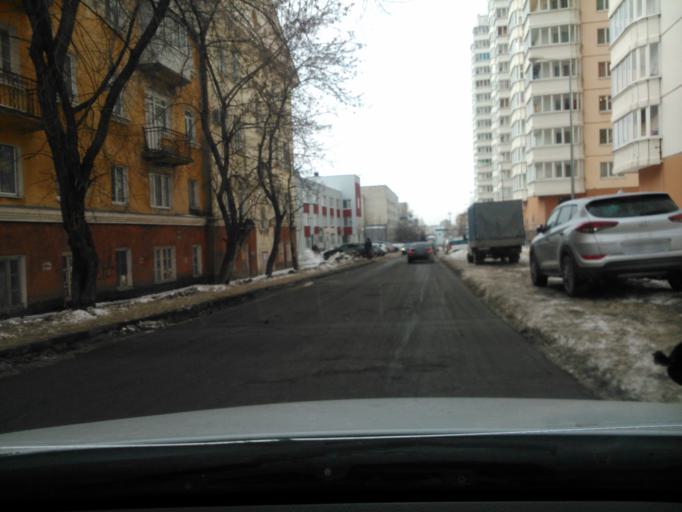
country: RU
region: Perm
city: Perm
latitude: 57.9993
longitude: 56.2372
